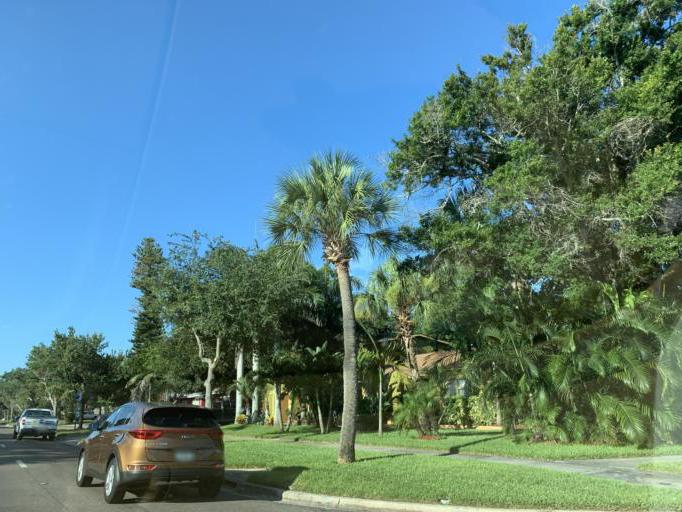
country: US
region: Florida
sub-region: Pinellas County
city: Saint Petersburg
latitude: 27.7431
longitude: -82.6466
